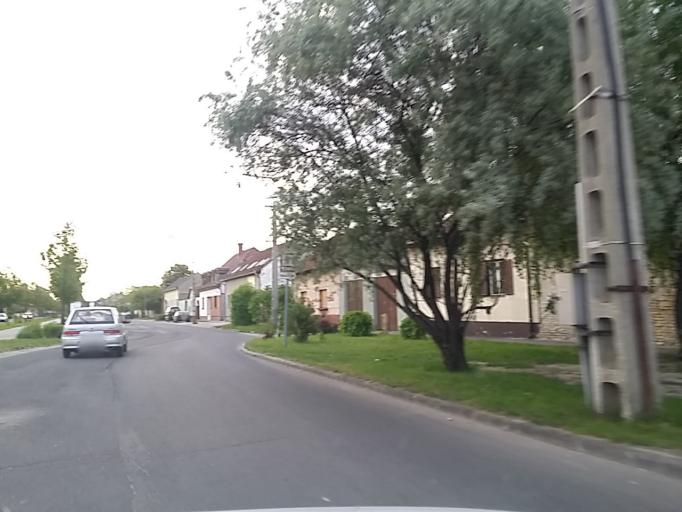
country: HU
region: Bacs-Kiskun
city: Kecskemet
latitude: 46.9021
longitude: 19.7048
